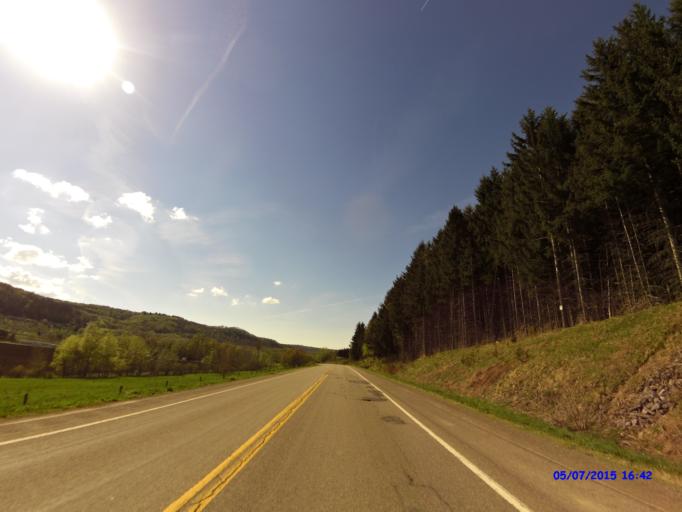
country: US
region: New York
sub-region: Cattaraugus County
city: Little Valley
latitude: 42.3024
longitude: -78.7120
